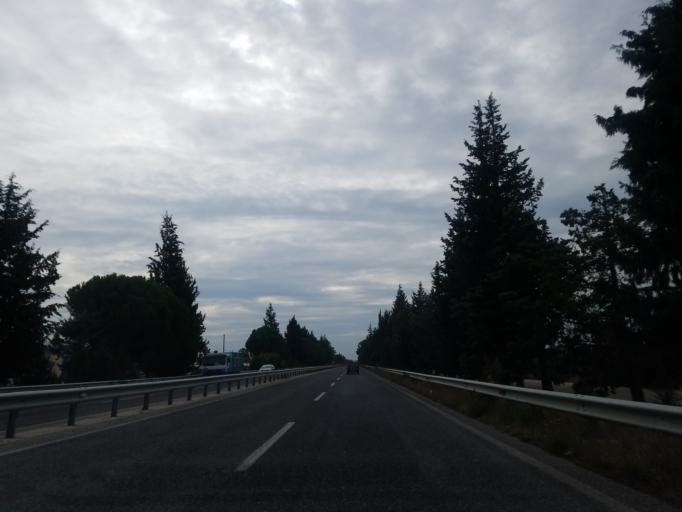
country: GR
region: Thessaly
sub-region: Trikala
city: Vasiliki
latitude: 39.6503
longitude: 21.6845
